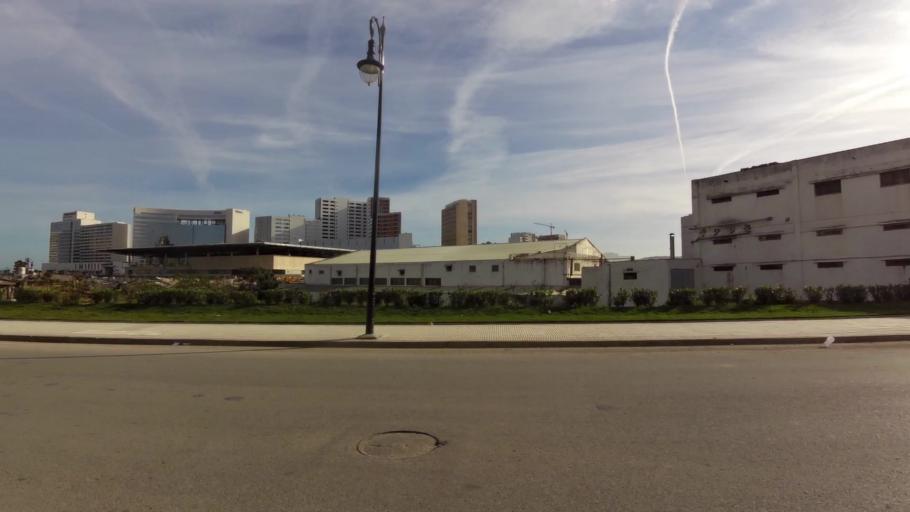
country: MA
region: Tanger-Tetouan
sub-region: Tanger-Assilah
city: Tangier
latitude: 35.7686
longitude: -5.7866
